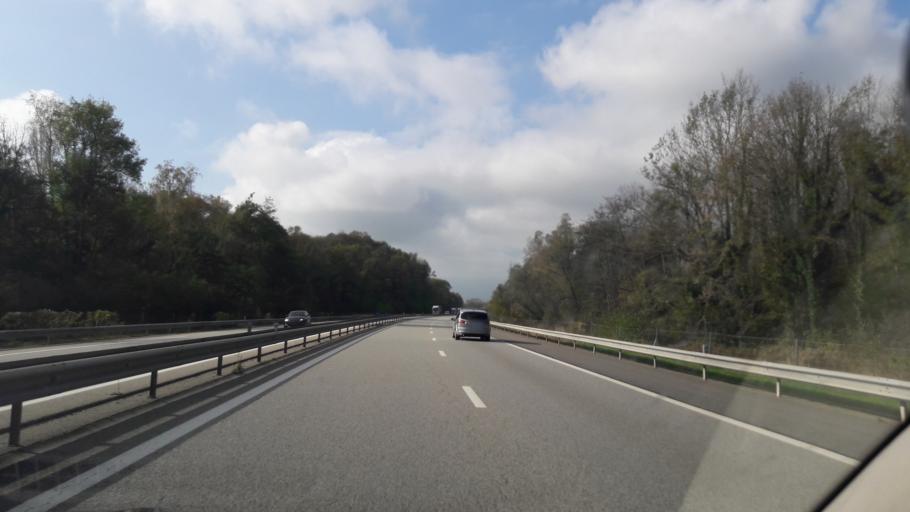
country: FR
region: Rhone-Alpes
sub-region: Departement de la Savoie
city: Cruet
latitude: 45.5094
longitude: 6.0970
